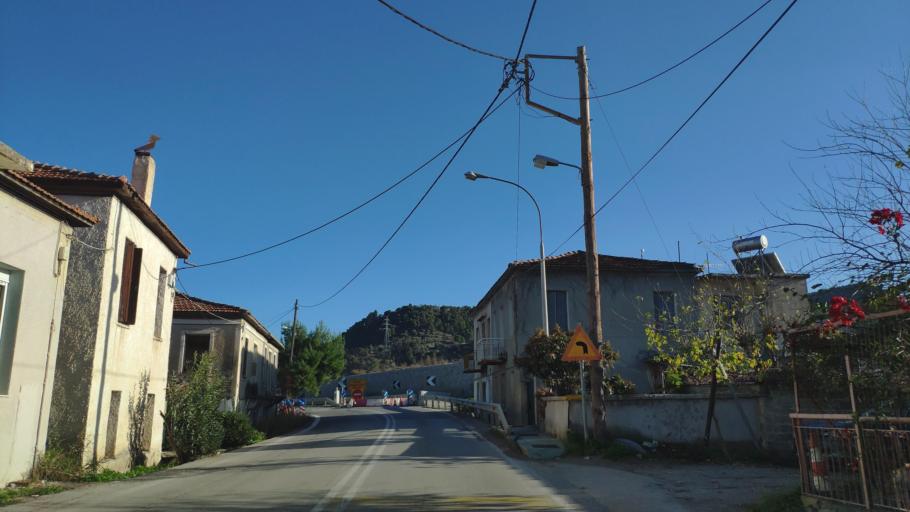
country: GR
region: Peloponnese
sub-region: Nomos Korinthias
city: Xylokastro
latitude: 38.0756
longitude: 22.6208
